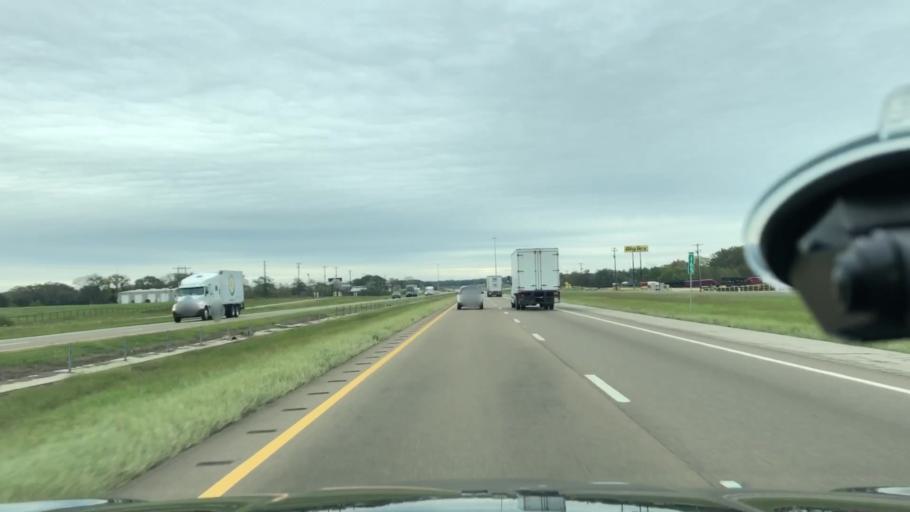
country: US
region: Texas
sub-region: Titus County
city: Mount Pleasant
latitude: 33.1937
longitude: -94.9305
